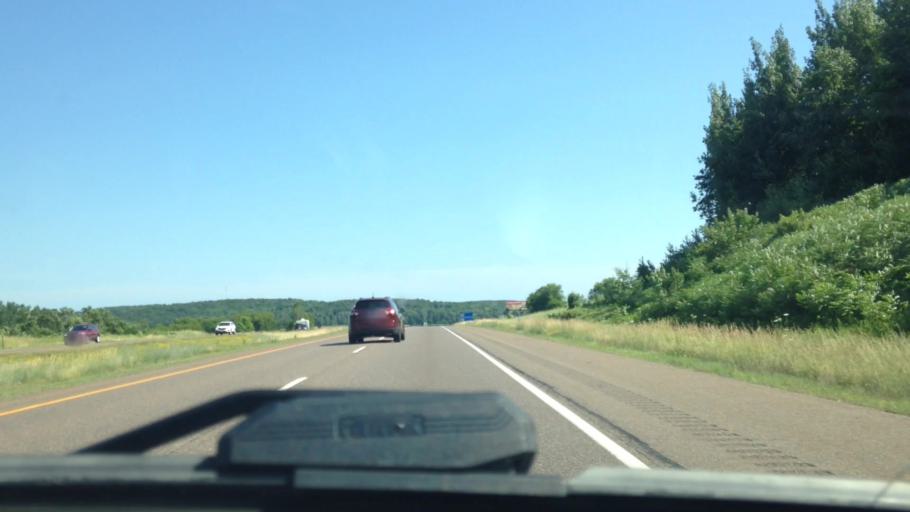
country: US
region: Wisconsin
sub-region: Chippewa County
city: Chippewa Falls
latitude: 44.9549
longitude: -91.4257
